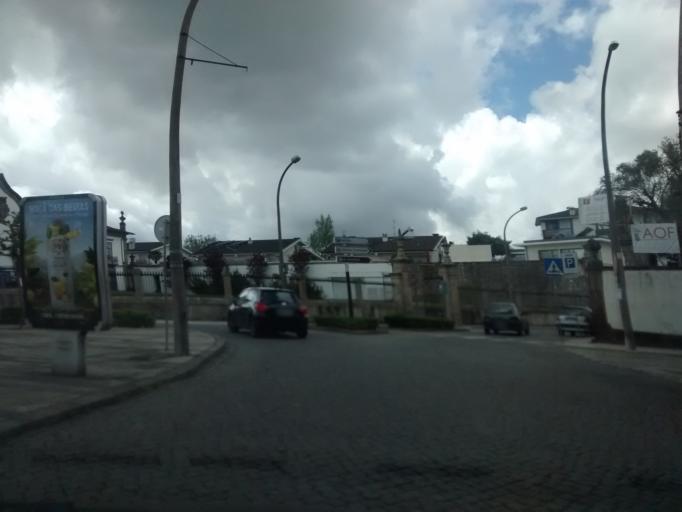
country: PT
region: Braga
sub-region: Braga
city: Braga
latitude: 41.5477
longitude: -8.4283
